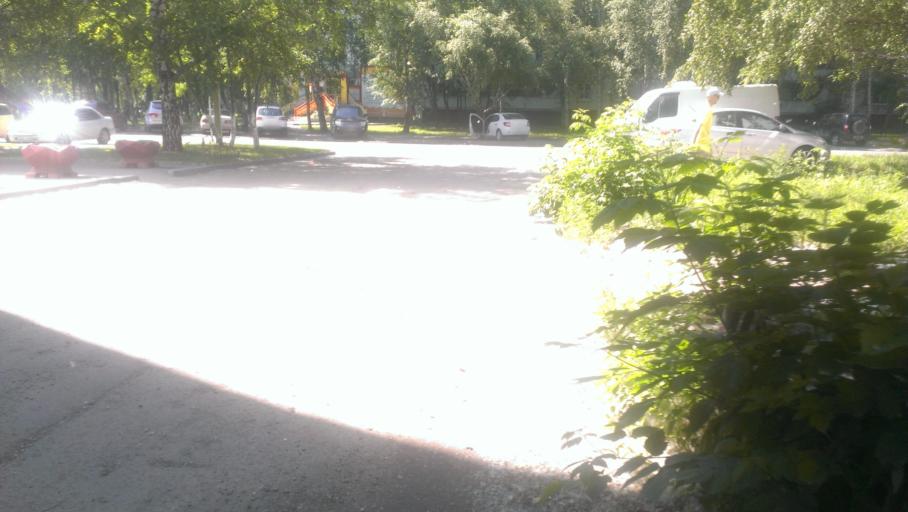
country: RU
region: Altai Krai
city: Novosilikatnyy
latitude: 53.3447
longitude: 83.6804
